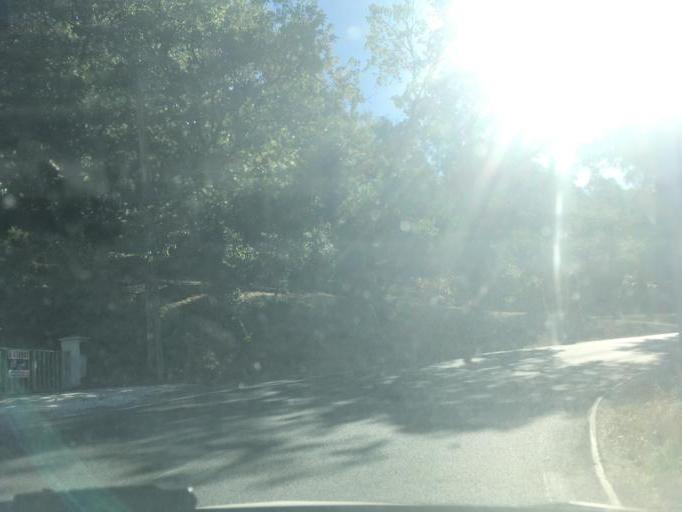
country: FR
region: Provence-Alpes-Cote d'Azur
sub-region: Departement du Var
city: La Garde-Freinet
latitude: 43.3263
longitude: 6.4741
